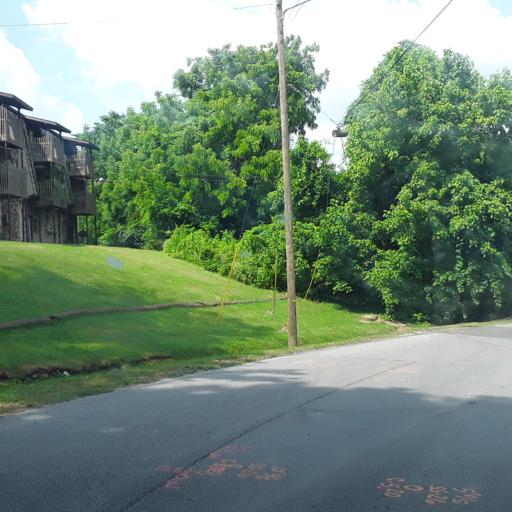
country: US
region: Tennessee
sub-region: Davidson County
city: Oak Hill
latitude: 36.1149
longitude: -86.7346
